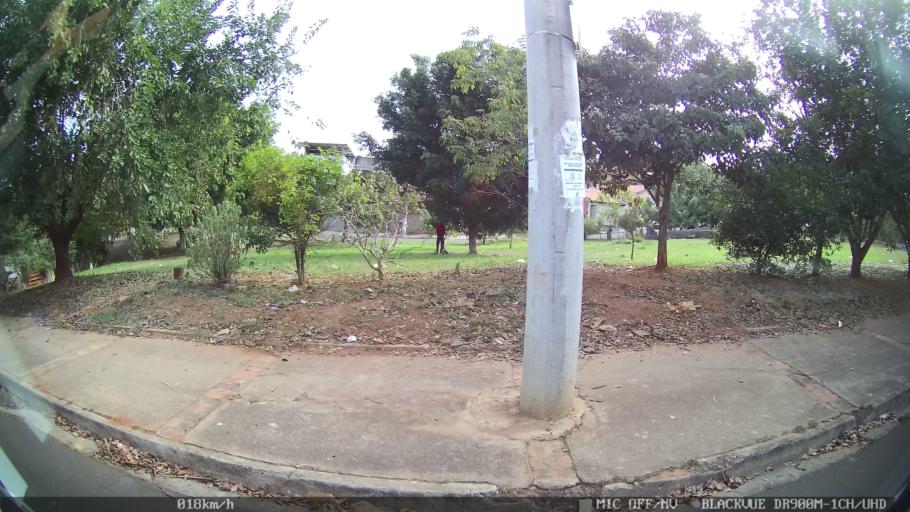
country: BR
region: Sao Paulo
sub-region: Santa Barbara D'Oeste
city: Santa Barbara d'Oeste
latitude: -22.7733
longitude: -47.3941
